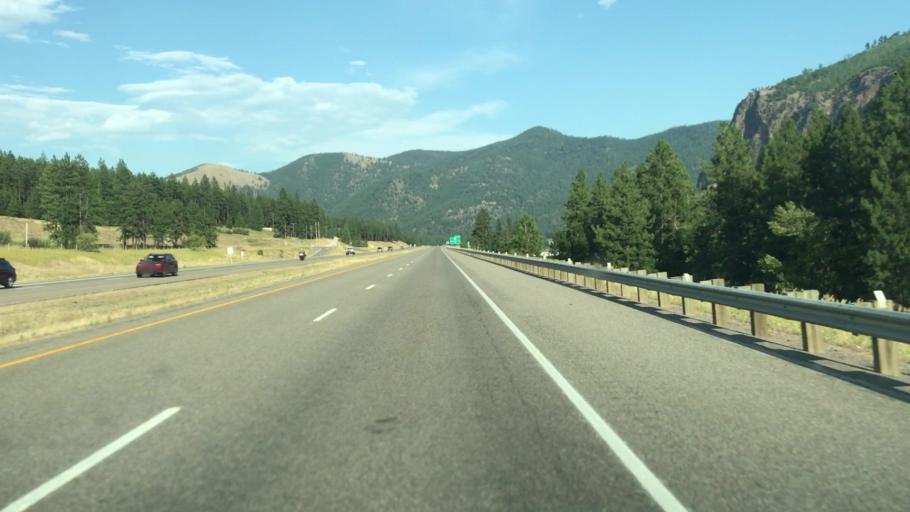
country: US
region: Montana
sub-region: Missoula County
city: Frenchtown
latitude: 46.9958
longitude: -114.4572
